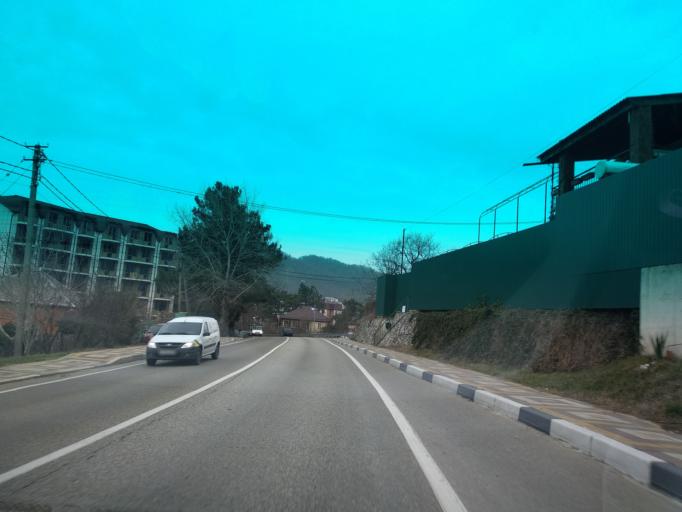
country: RU
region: Krasnodarskiy
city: Ol'ginka
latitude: 44.1964
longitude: 38.8918
